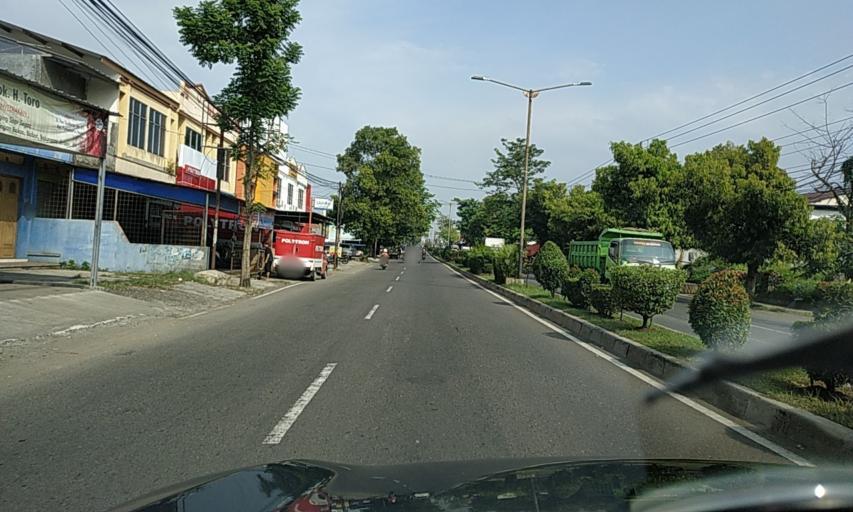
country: ID
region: Central Java
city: Purwokerto
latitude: -7.4217
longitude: 109.2087
